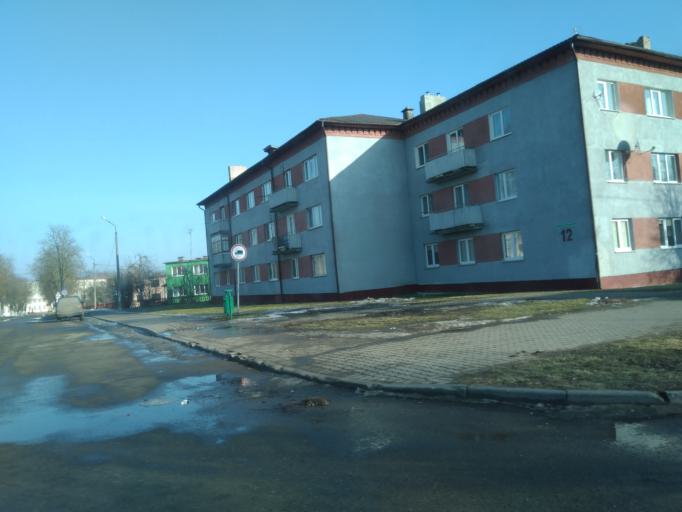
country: BY
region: Minsk
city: Snow
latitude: 53.2213
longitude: 26.4004
